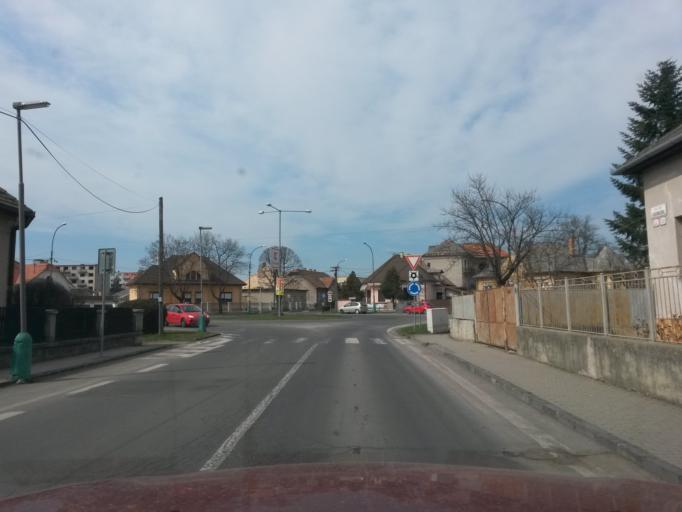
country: SK
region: Banskobystricky
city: Lucenec
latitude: 48.3331
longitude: 19.6581
